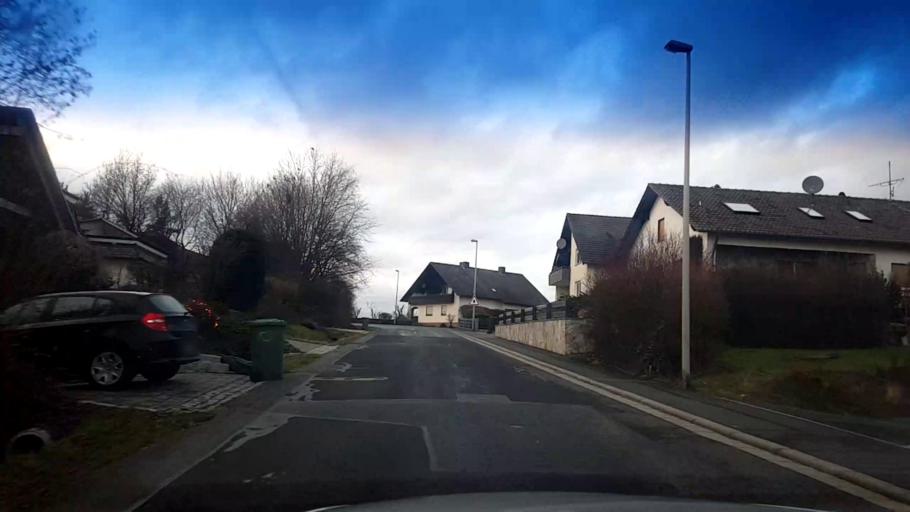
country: DE
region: Bavaria
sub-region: Upper Franconia
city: Strullendorf
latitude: 49.8608
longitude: 11.0072
